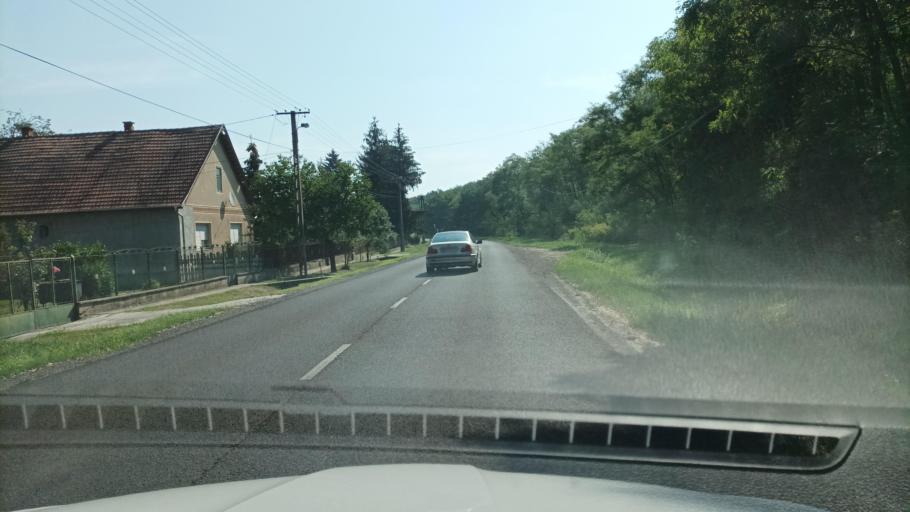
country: HU
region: Pest
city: Valko
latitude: 47.5688
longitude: 19.4836
